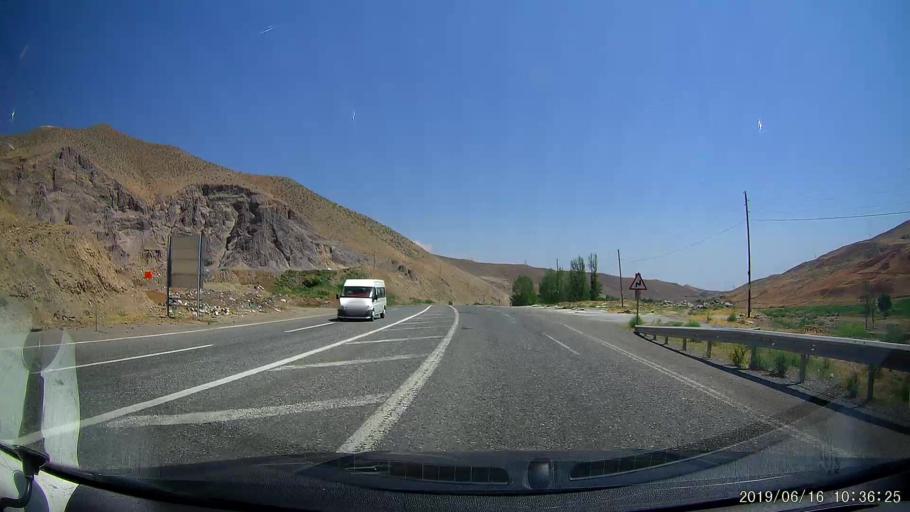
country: TR
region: Igdir
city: Tuzluca
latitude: 40.0376
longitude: 43.6803
